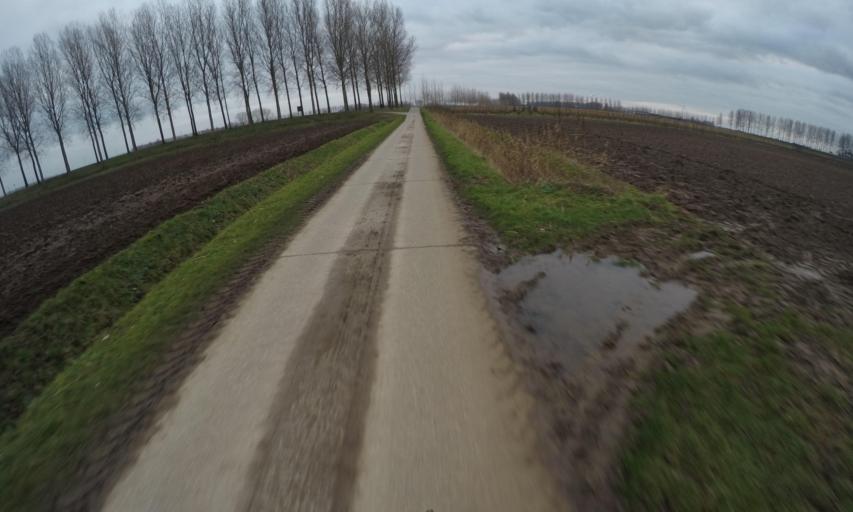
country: BE
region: Flanders
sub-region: Provincie Oost-Vlaanderen
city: Sint-Gillis-Waas
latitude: 51.2509
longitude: 4.1272
